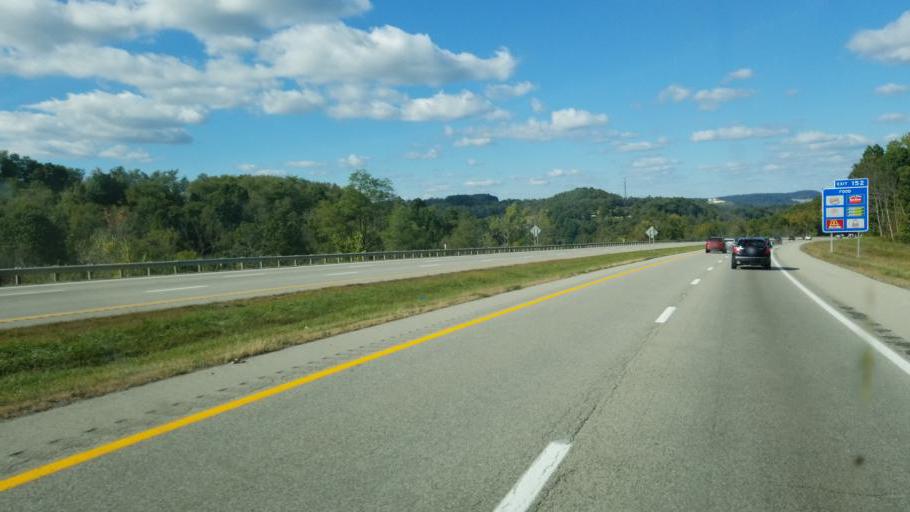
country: US
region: West Virginia
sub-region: Monongalia County
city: Westover
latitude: 39.6076
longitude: -79.9933
